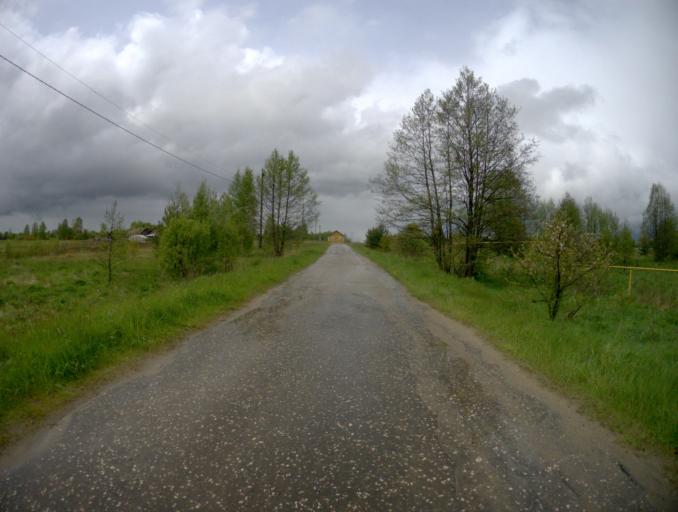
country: RU
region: Vladimir
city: Velikodvorskiy
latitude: 55.3713
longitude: 40.8594
